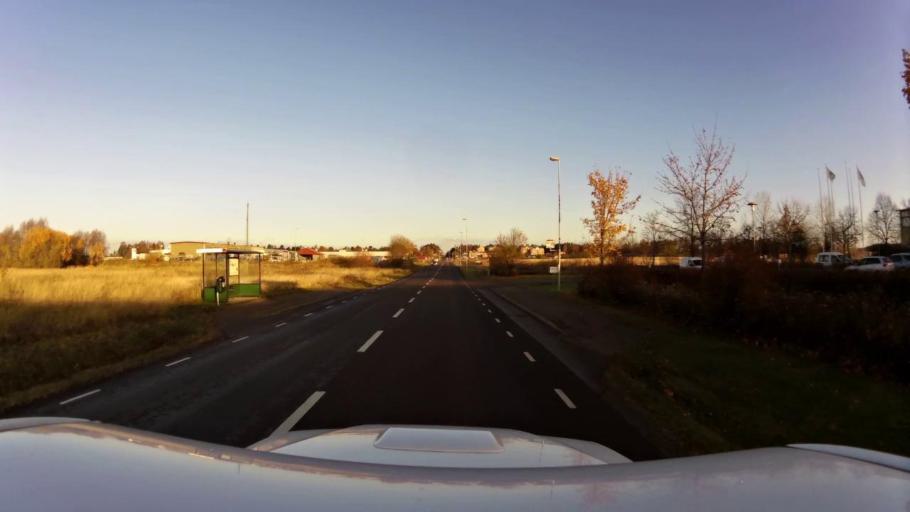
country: SE
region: OEstergoetland
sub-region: Linkopings Kommun
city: Linkoping
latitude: 58.4205
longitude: 15.6798
